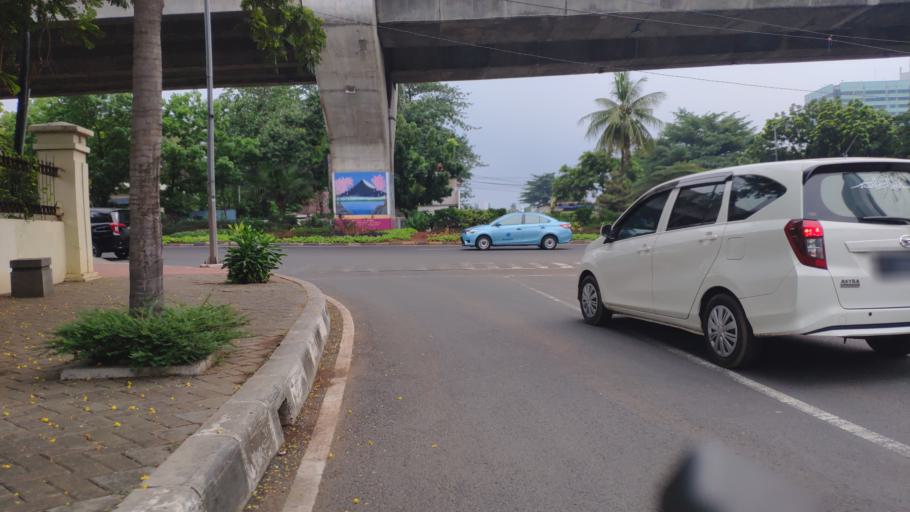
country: ID
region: Jakarta Raya
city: Jakarta
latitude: -6.2252
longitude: 106.8357
